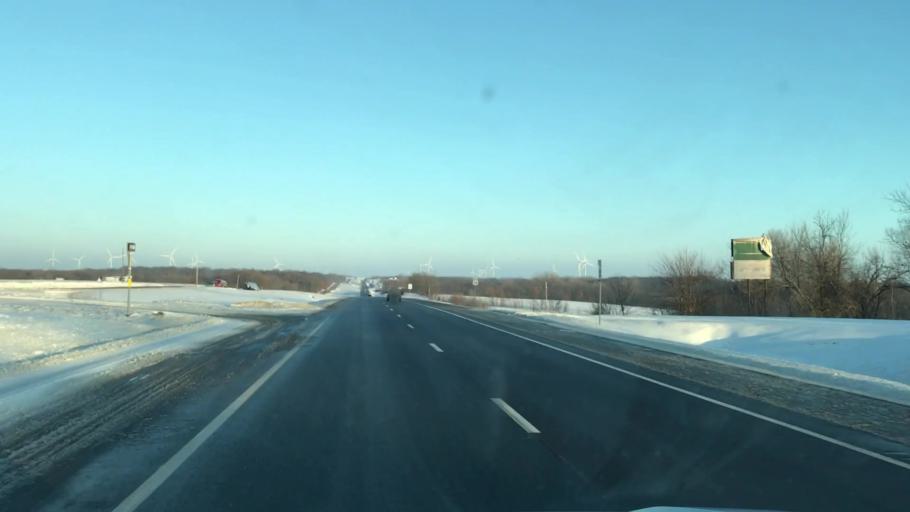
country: US
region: Missouri
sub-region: DeKalb County
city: Maysville
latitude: 39.7620
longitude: -94.4943
